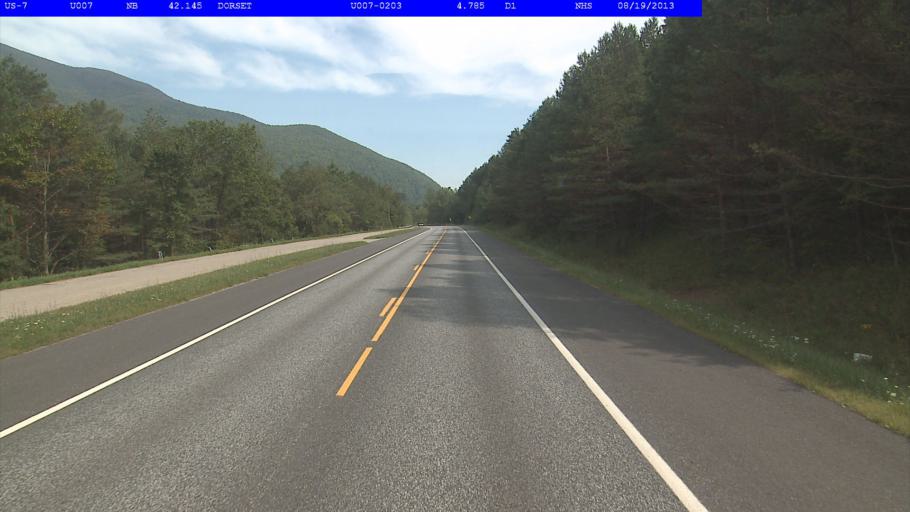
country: US
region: Vermont
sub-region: Bennington County
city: Manchester Center
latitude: 43.2777
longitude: -73.0034
